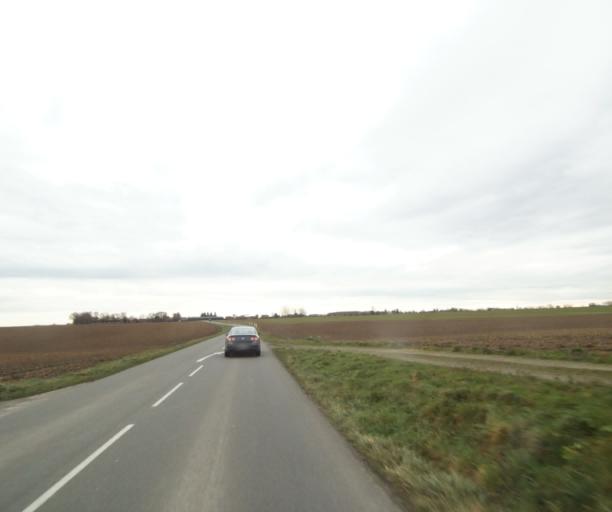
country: FR
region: Nord-Pas-de-Calais
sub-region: Departement du Nord
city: Sebourg
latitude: 50.3517
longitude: 3.6261
